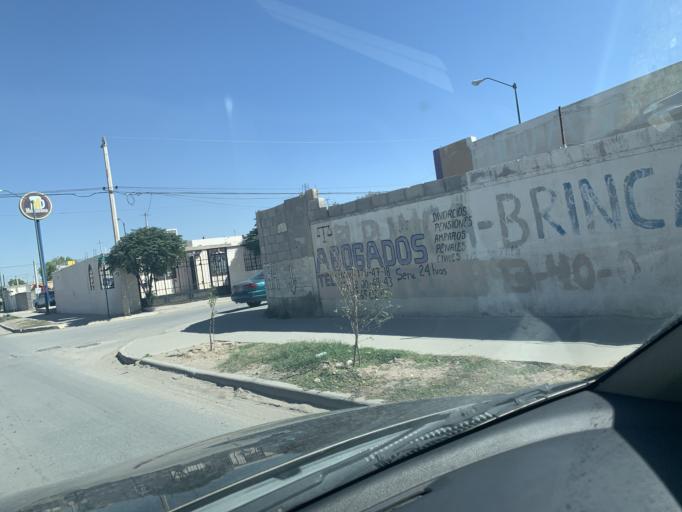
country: US
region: Texas
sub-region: El Paso County
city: Socorro Mission Number 1 Colonia
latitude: 31.5980
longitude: -106.3596
